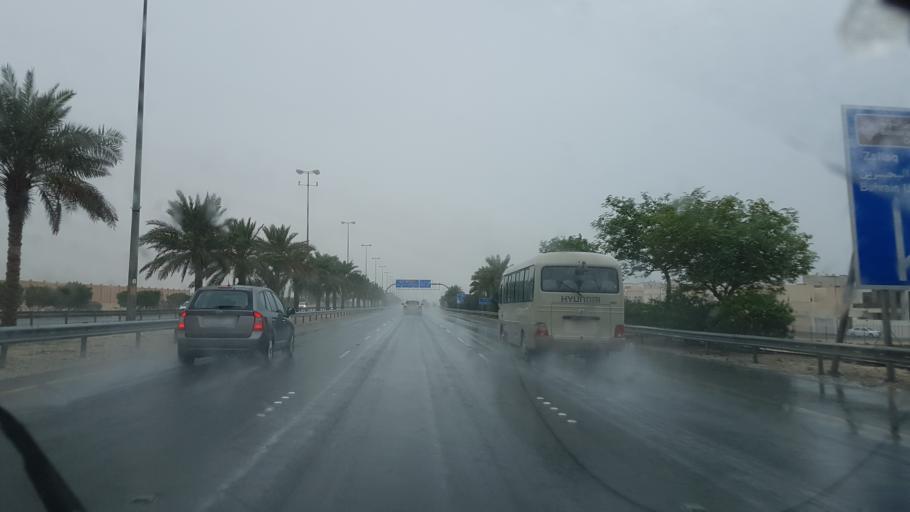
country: BH
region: Central Governorate
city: Madinat Hamad
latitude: 26.1089
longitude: 50.5112
